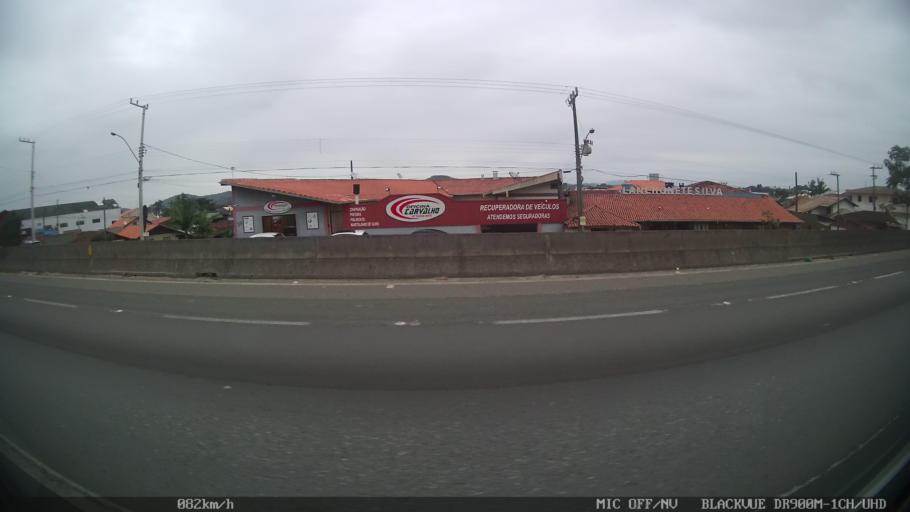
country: BR
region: Santa Catarina
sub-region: Barra Velha
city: Barra Velha
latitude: -26.6462
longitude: -48.6877
